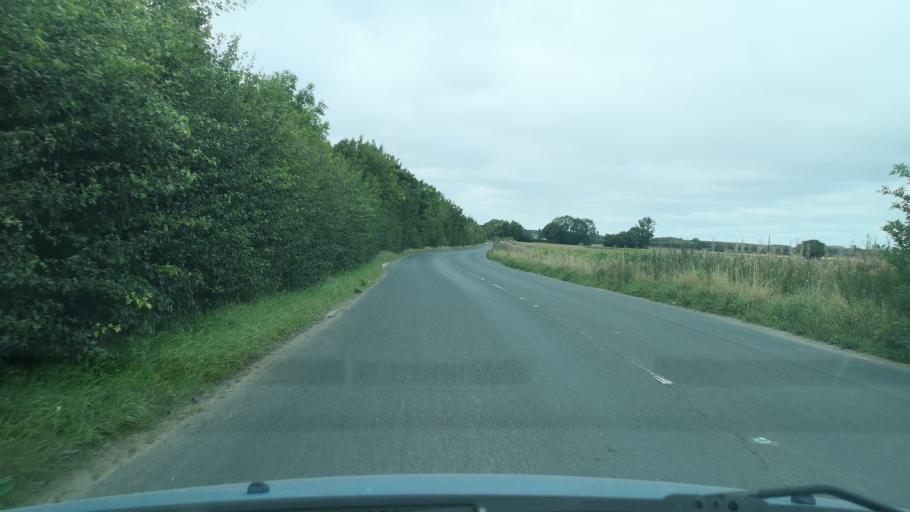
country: GB
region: England
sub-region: City and Borough of Wakefield
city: Knottingley
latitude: 53.6911
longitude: -1.2032
